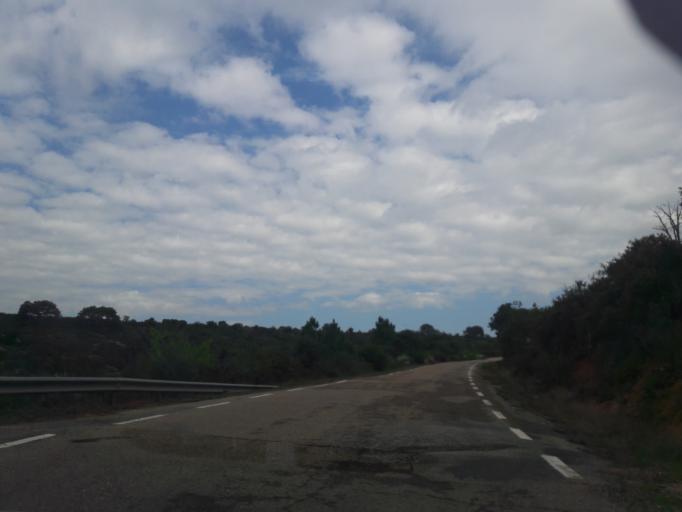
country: ES
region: Castille and Leon
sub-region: Provincia de Salamanca
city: Serradilla del Arroyo
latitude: 40.5288
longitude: -6.3846
